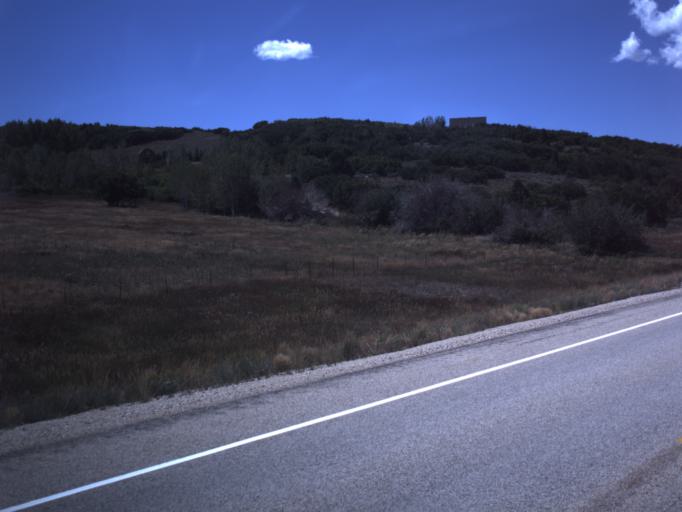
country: US
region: Utah
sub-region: Summit County
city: Francis
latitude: 40.5953
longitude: -111.3671
